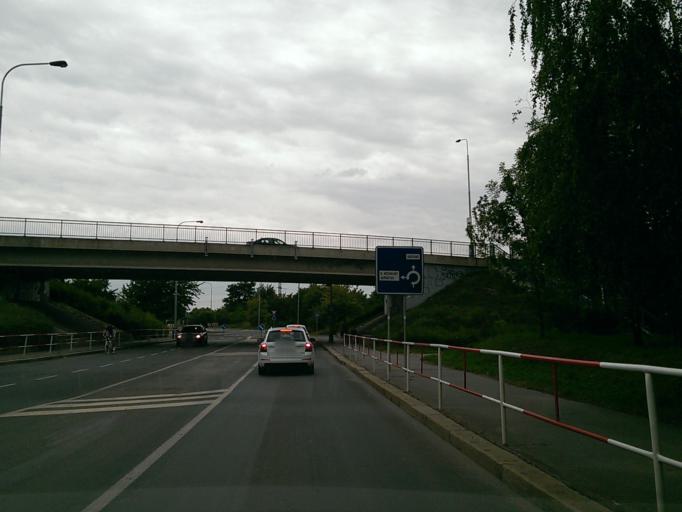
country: CZ
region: Praha
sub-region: Praha 14
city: Dolni Pocernice
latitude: 50.0482
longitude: 14.5648
